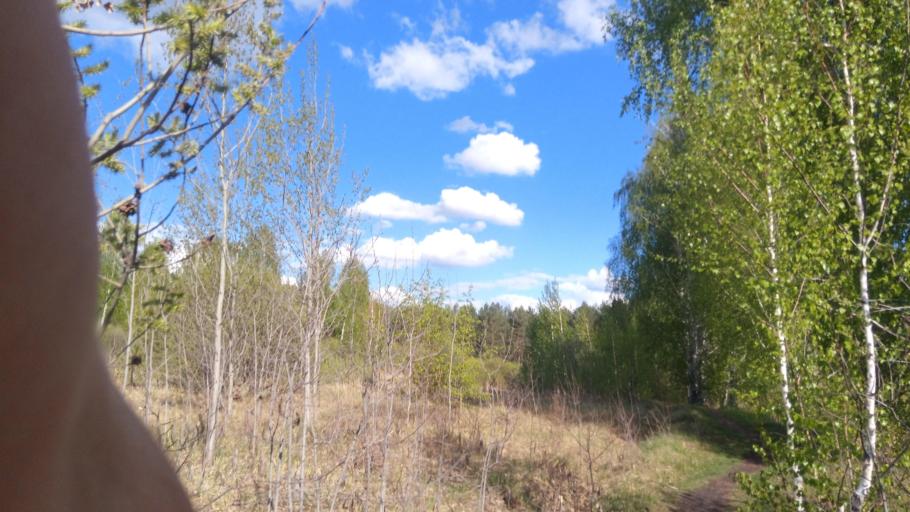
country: RU
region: Chelyabinsk
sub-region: Gorod Chelyabinsk
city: Chelyabinsk
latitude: 55.1582
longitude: 61.3194
